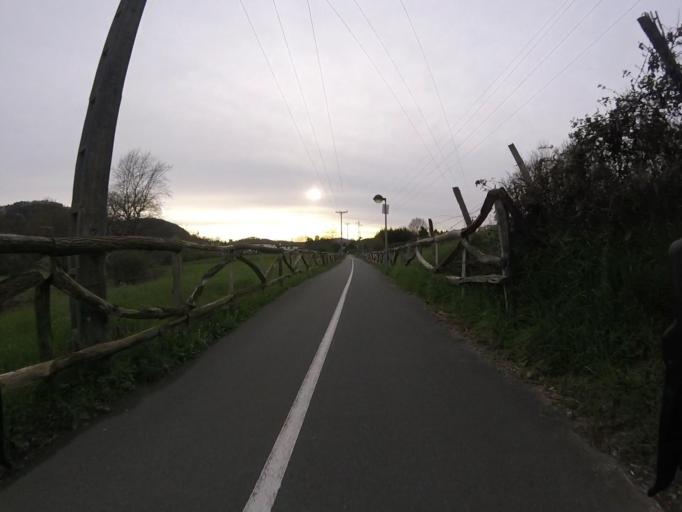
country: ES
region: Basque Country
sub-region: Provincia de Guipuzcoa
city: Lezo
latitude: 43.2946
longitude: -1.8520
